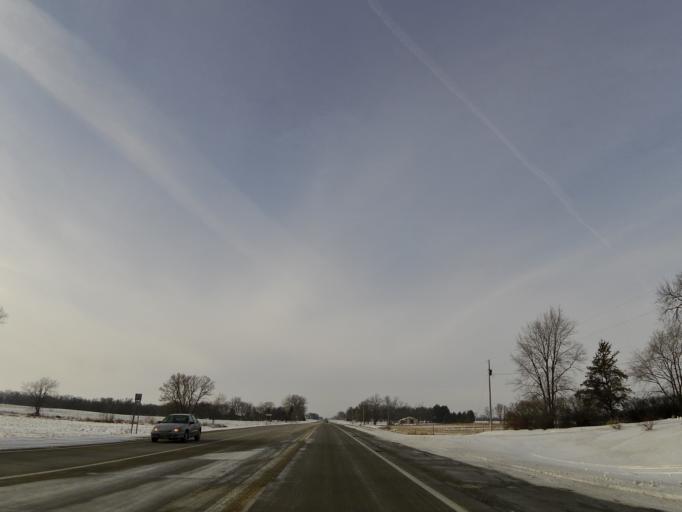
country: US
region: Minnesota
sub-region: McLeod County
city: Hutchinson
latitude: 44.8926
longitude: -94.2772
